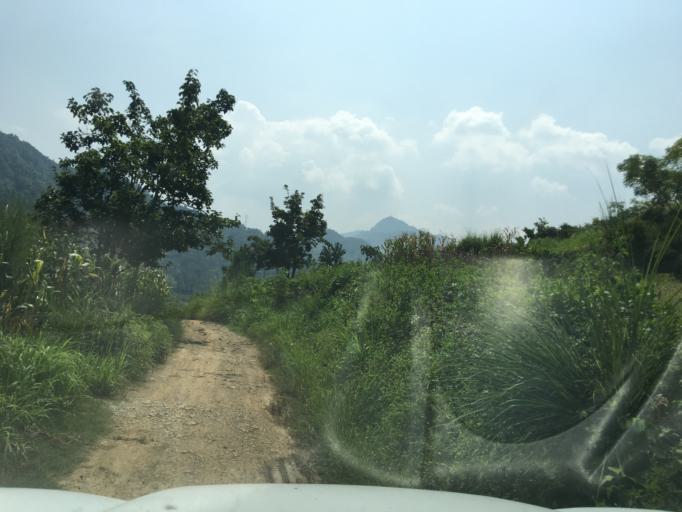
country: CN
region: Guangxi Zhuangzu Zizhiqu
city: Xinzhou
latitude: 24.9957
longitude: 105.7500
